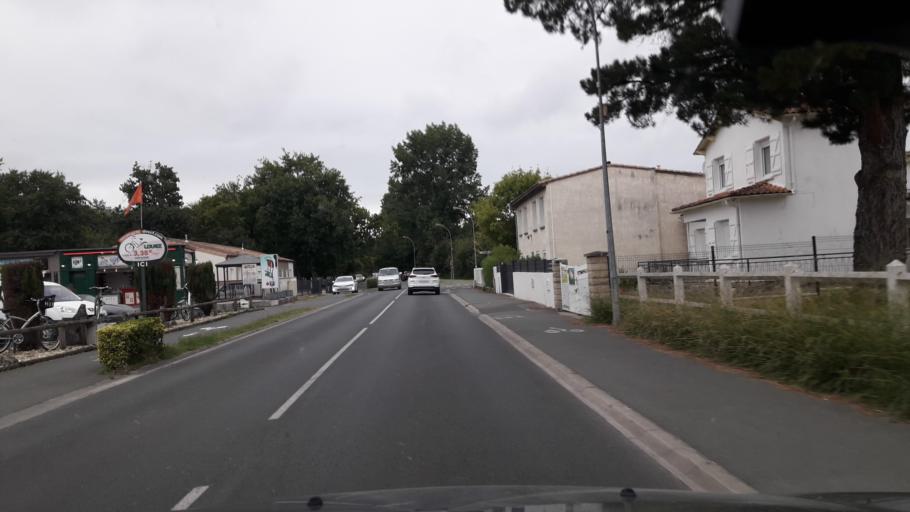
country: FR
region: Poitou-Charentes
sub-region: Departement de la Charente-Maritime
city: Les Mathes
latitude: 45.7151
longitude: -1.1555
